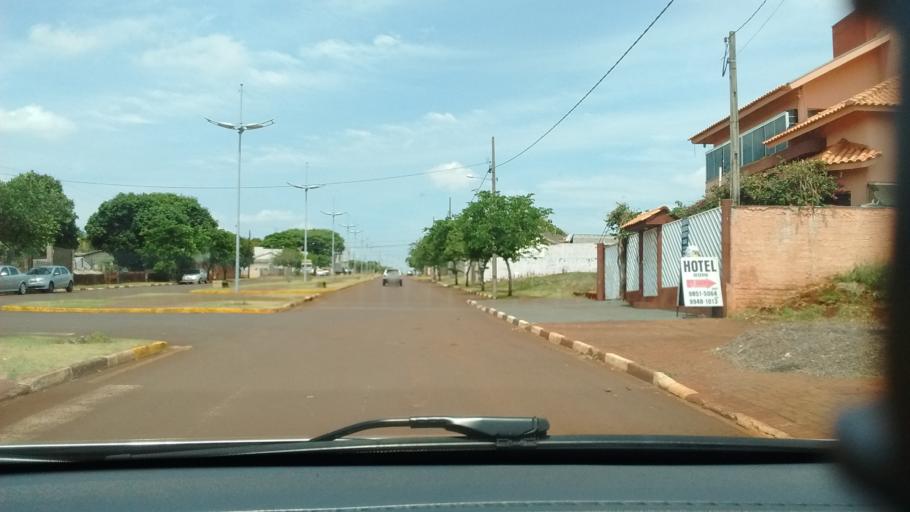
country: BR
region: Parana
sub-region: Corbelia
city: Corbelia
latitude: -24.5505
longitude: -52.9914
